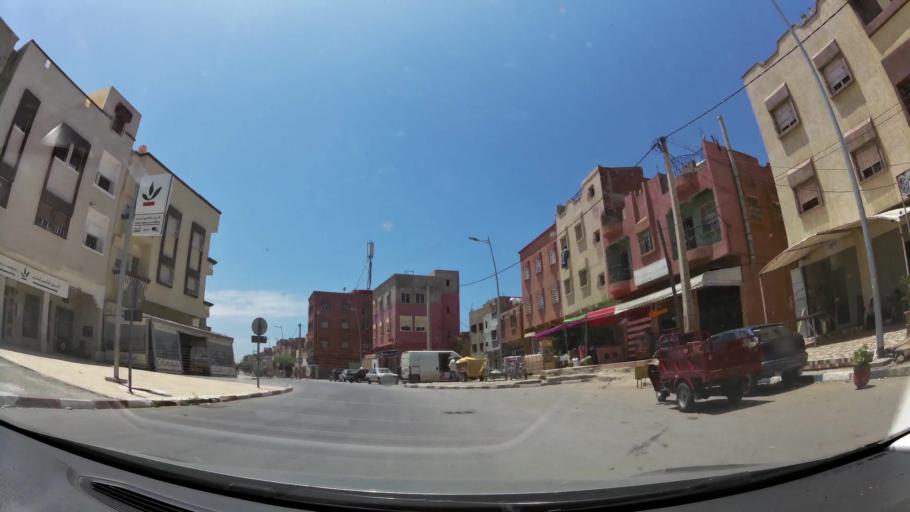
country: MA
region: Gharb-Chrarda-Beni Hssen
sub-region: Kenitra Province
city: Kenitra
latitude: 34.2598
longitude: -6.6477
